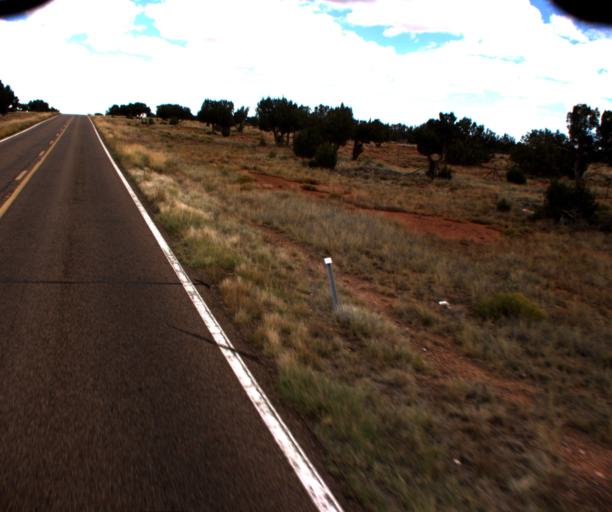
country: US
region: Arizona
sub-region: Navajo County
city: Heber-Overgaard
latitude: 34.5327
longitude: -110.4243
